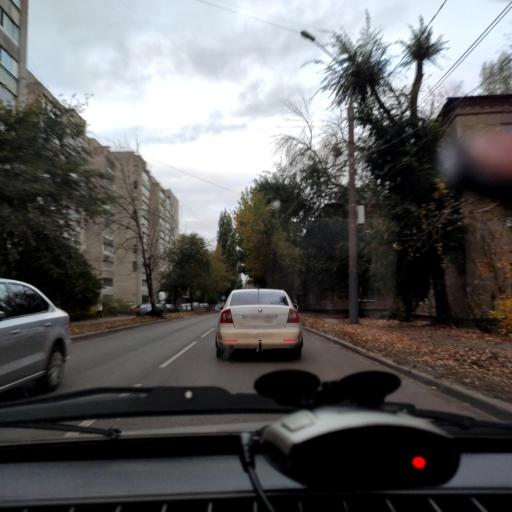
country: RU
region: Voronezj
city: Voronezh
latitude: 51.6459
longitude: 39.1733
